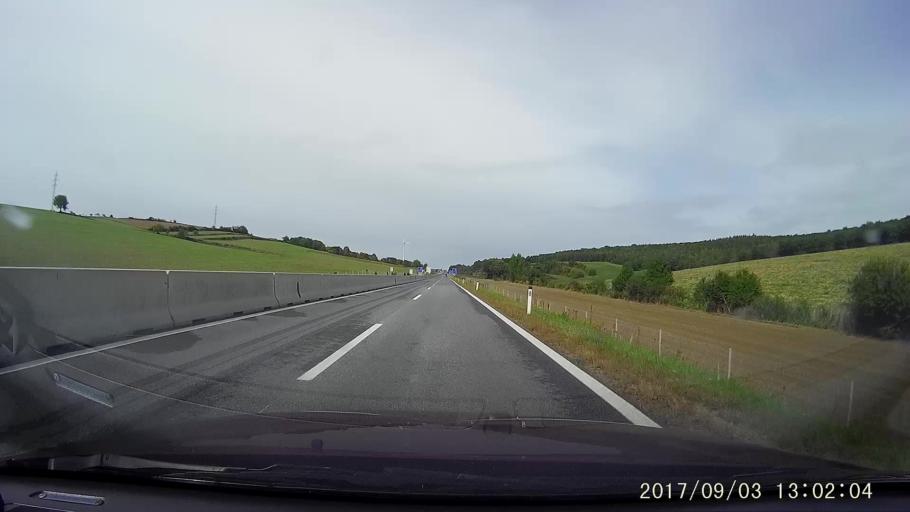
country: AT
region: Lower Austria
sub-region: Politischer Bezirk Hollabrunn
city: Hollabrunn
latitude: 48.5154
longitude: 16.0873
